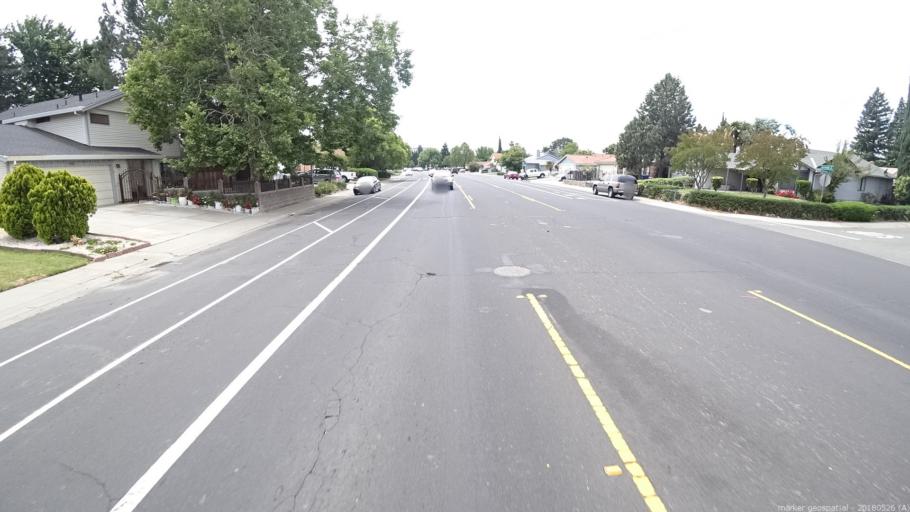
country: US
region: California
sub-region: Sacramento County
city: Sacramento
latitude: 38.6217
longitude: -121.5105
